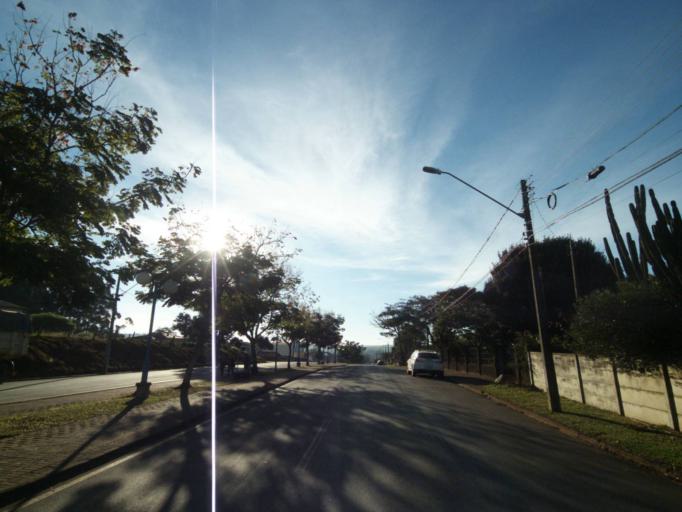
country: BR
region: Parana
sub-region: Tibagi
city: Tibagi
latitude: -24.5225
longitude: -50.4099
